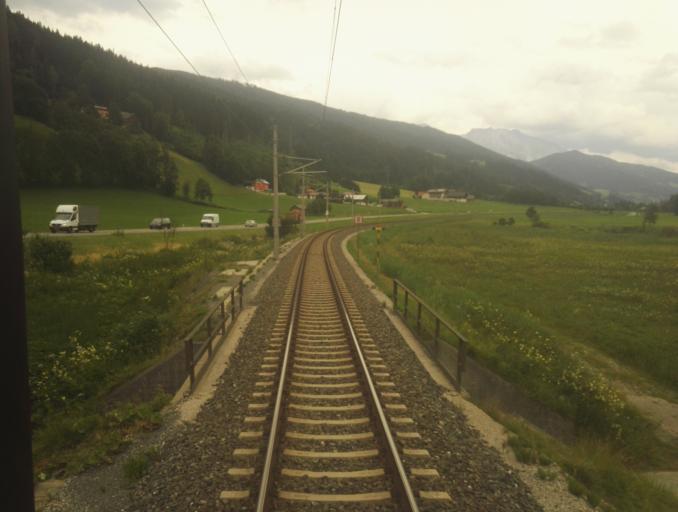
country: AT
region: Salzburg
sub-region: Politischer Bezirk Sankt Johann im Pongau
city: Forstau
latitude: 47.3886
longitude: 13.4960
